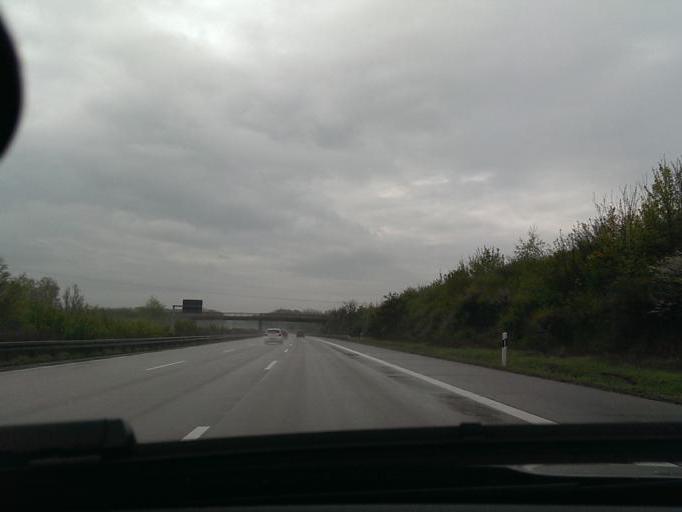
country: DE
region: Lower Saxony
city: Laatzen
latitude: 52.3295
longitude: 9.8632
